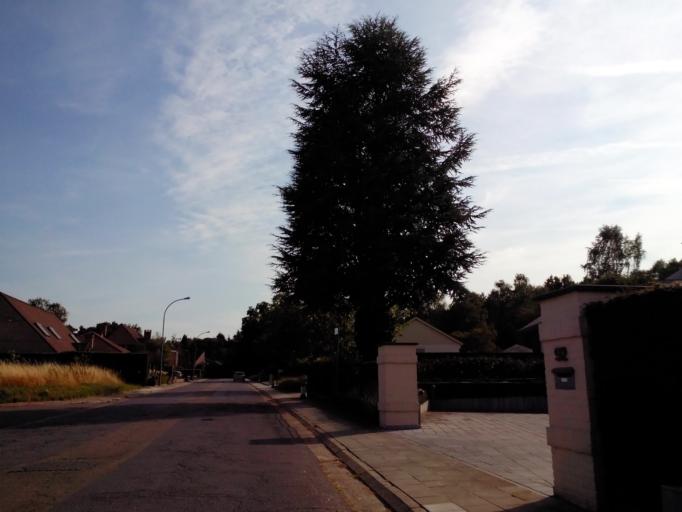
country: BE
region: Flanders
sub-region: Provincie Vlaams-Brabant
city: Leuven
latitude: 50.8538
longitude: 4.6914
